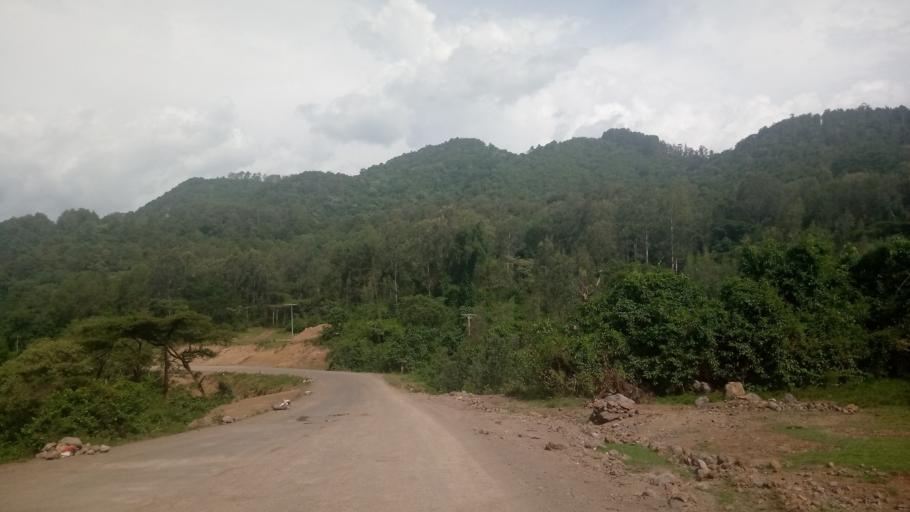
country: ET
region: Oromiya
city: Agaro
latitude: 8.0432
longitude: 36.4671
